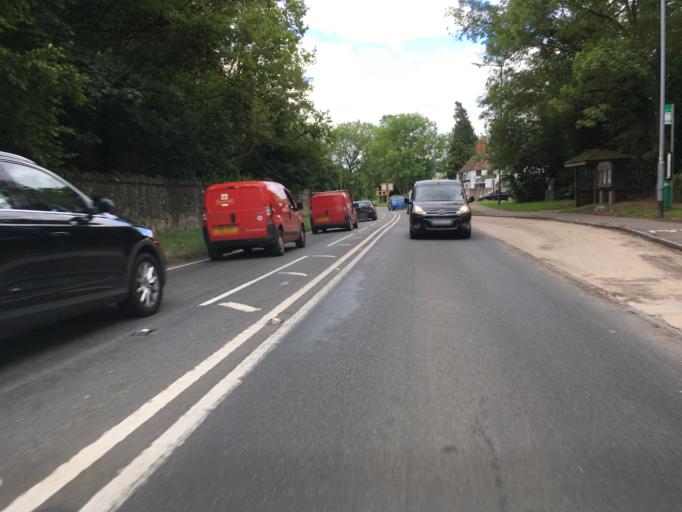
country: GB
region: England
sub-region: Buckinghamshire
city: Stone
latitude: 51.8021
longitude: -0.8490
